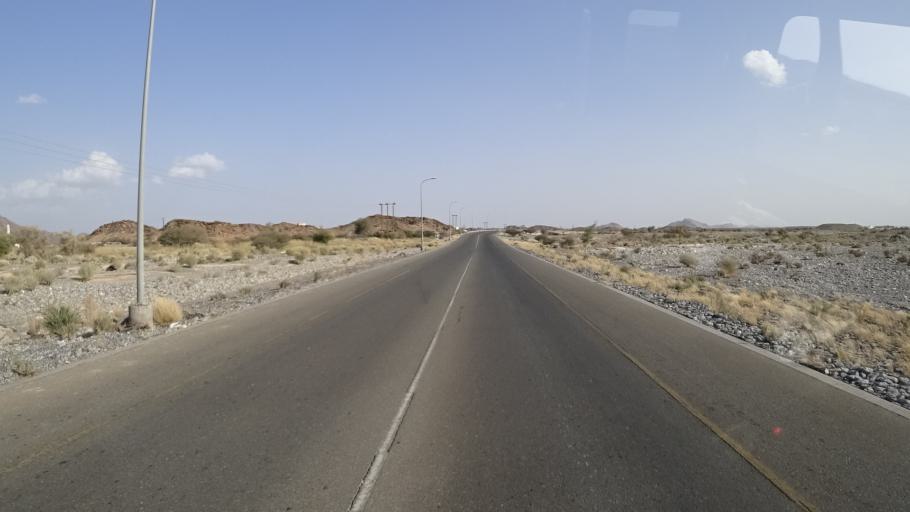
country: OM
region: Muhafazat ad Dakhiliyah
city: Izki
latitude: 22.8767
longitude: 57.7572
